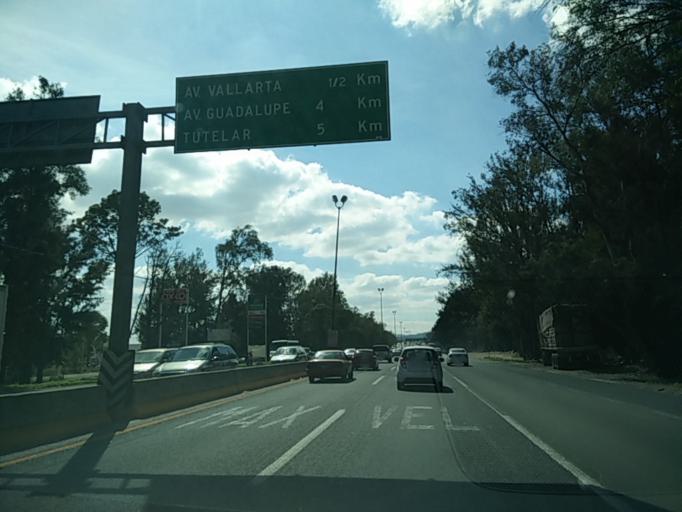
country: MX
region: Jalisco
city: Zapopan2
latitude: 20.7042
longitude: -103.4484
